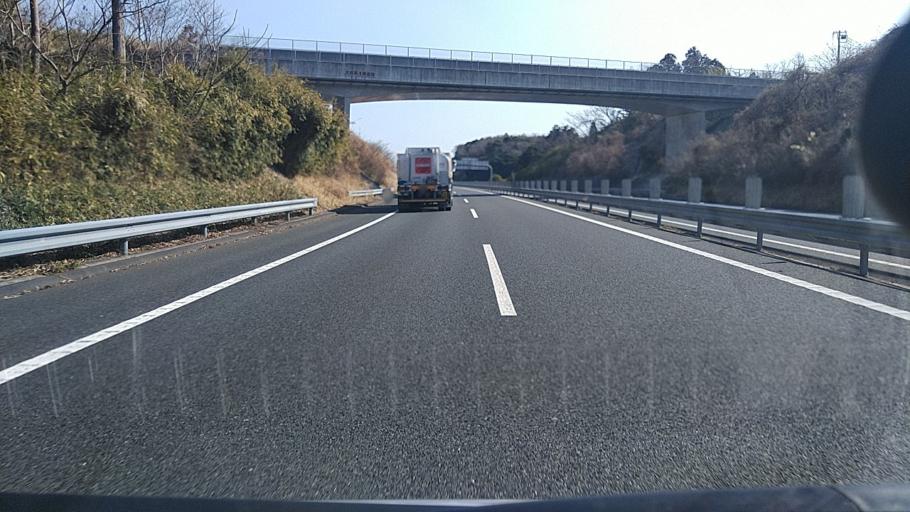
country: JP
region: Chiba
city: Kisarazu
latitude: 35.3672
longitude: 139.9893
